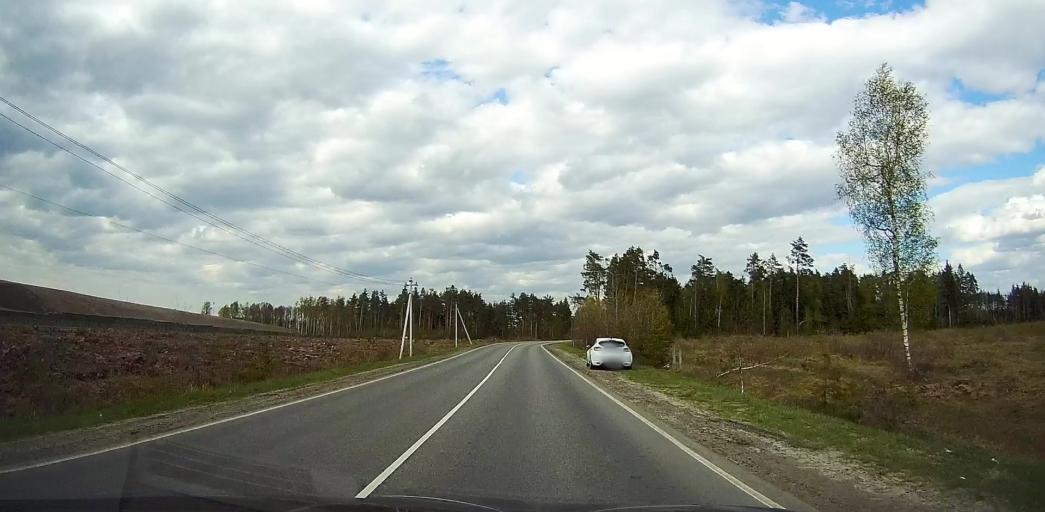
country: RU
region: Moskovskaya
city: Rakhmanovo
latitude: 55.7275
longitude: 38.6298
